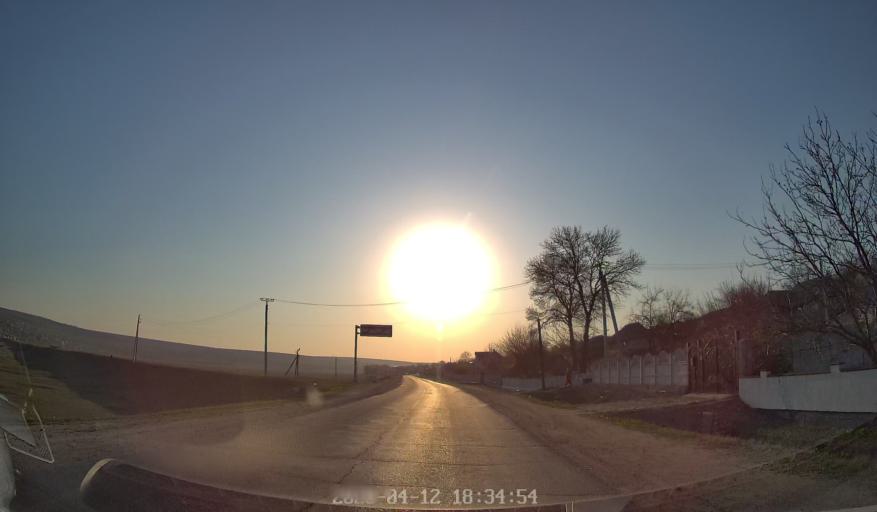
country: MD
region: Chisinau
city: Vadul lui Voda
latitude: 47.1169
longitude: 29.0555
